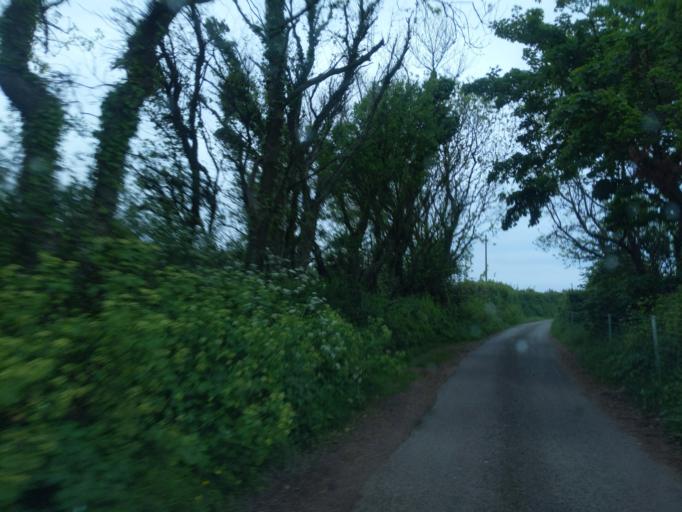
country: GB
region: England
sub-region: Borough of Torbay
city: Brixham
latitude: 50.3620
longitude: -3.5310
